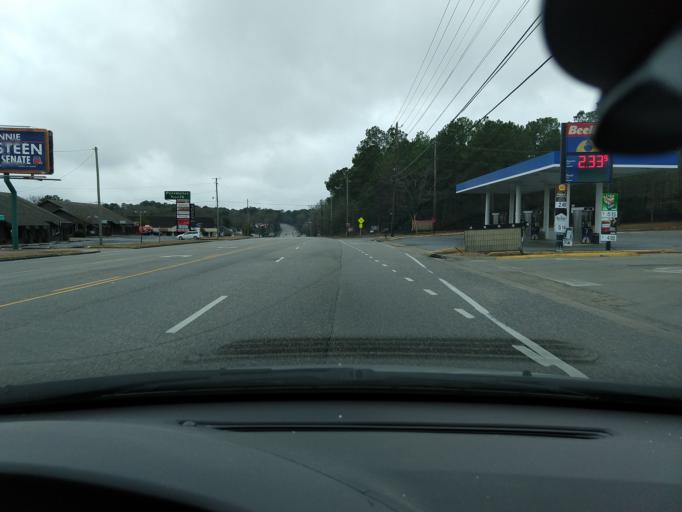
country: US
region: Alabama
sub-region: Houston County
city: Dothan
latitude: 31.2563
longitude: -85.4341
